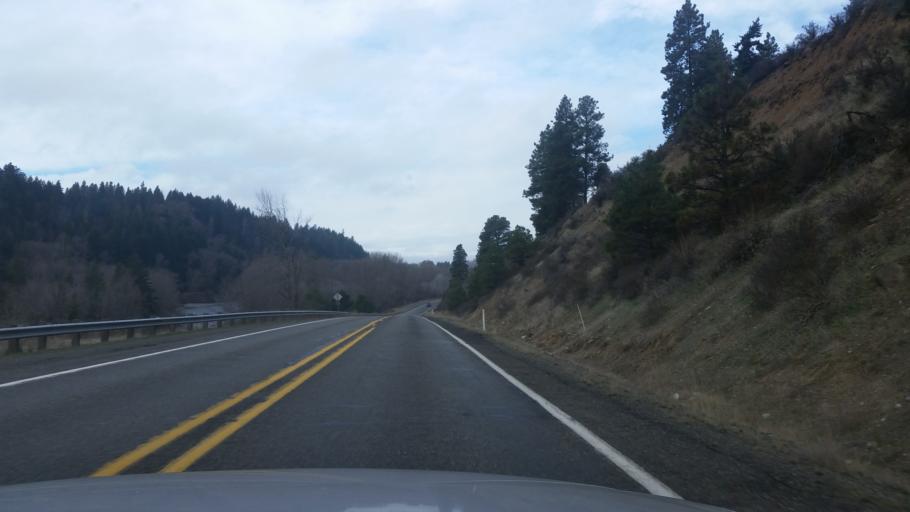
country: US
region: Washington
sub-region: Kittitas County
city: Cle Elum
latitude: 47.1662
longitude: -120.8232
